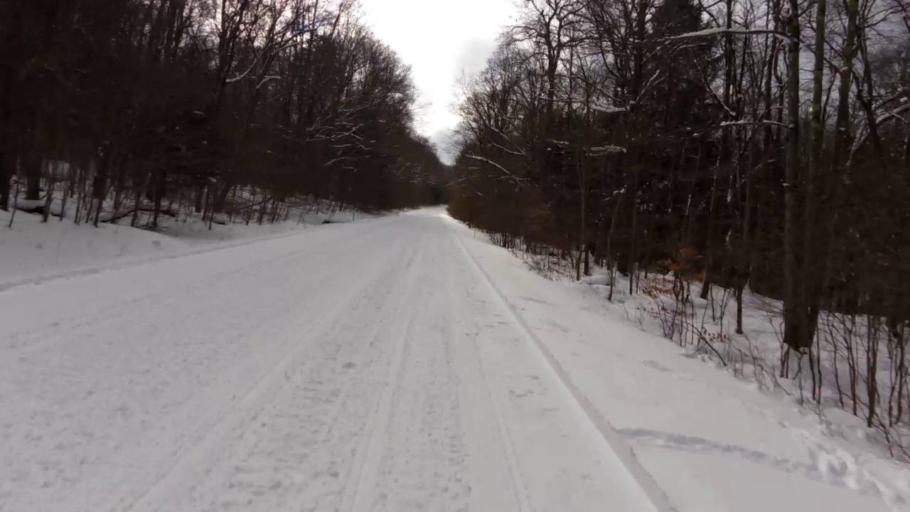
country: US
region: New York
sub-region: Cattaraugus County
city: Salamanca
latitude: 42.0830
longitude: -78.7484
